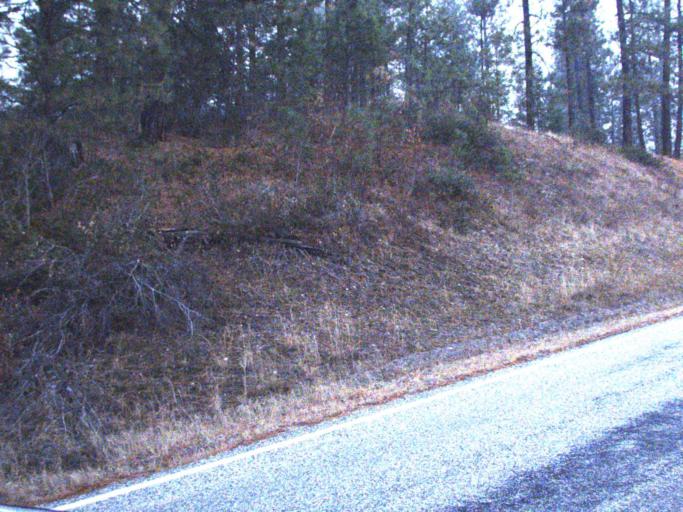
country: CA
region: British Columbia
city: Grand Forks
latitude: 48.9821
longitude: -118.2244
